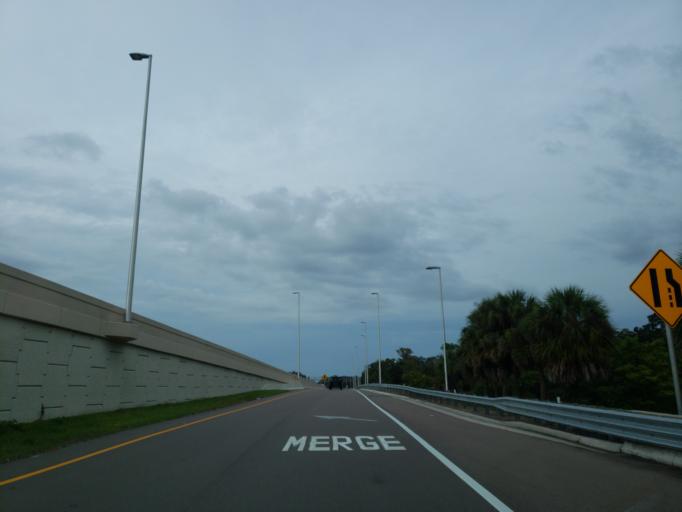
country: US
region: Florida
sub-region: Hillsborough County
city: Citrus Park
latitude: 28.0668
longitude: -82.5665
